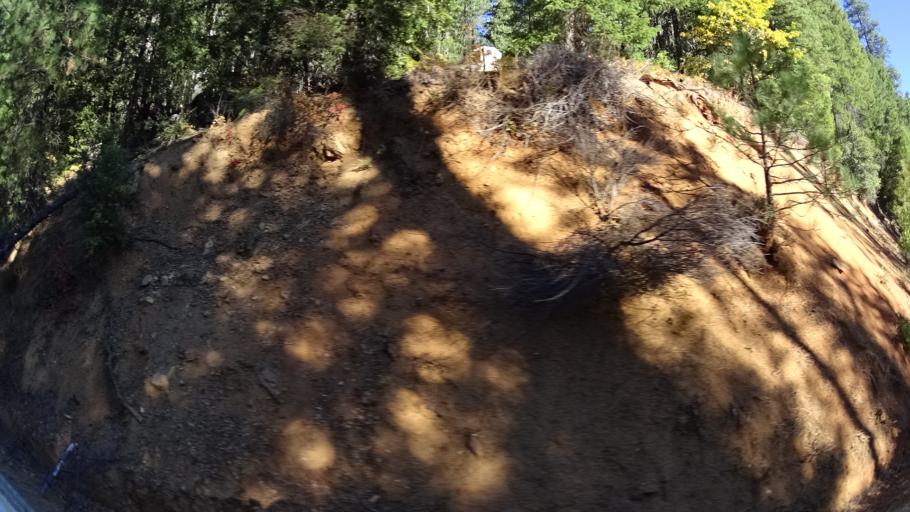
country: US
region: California
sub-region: Trinity County
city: Weaverville
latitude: 41.2227
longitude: -123.0184
